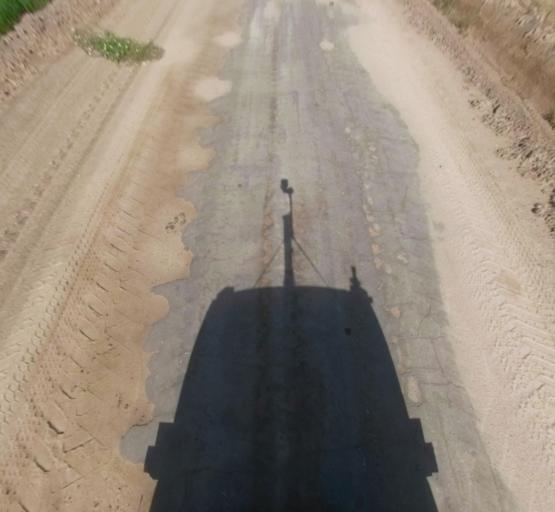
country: US
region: California
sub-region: Madera County
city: Chowchilla
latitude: 37.1273
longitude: -120.2910
